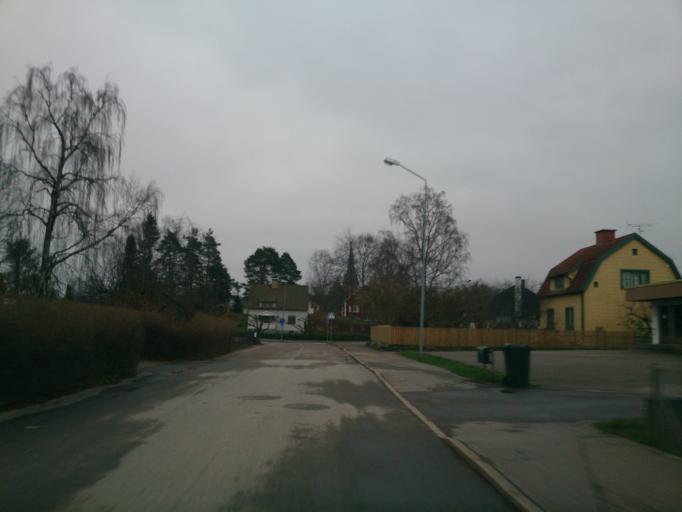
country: SE
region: OEstergoetland
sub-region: Atvidabergs Kommun
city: Atvidaberg
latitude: 58.1995
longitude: 15.9902
